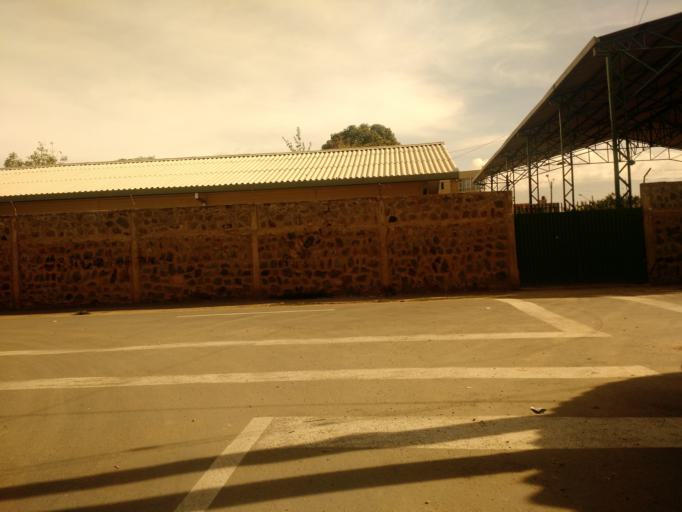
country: BO
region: Cochabamba
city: Cochabamba
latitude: -17.4287
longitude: -66.1574
